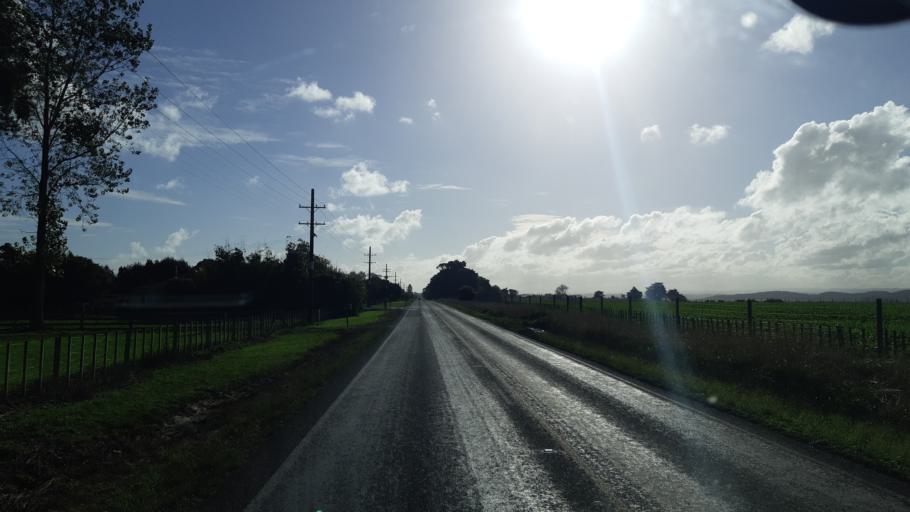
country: NZ
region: Manawatu-Wanganui
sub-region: Wanganui District
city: Wanganui
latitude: -39.9525
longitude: 175.1616
